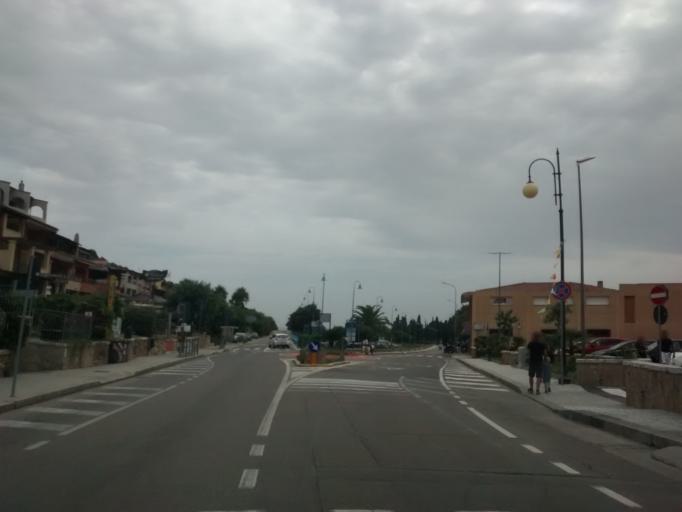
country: IT
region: Sardinia
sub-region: Provincia di Cagliari
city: Villasimius
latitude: 39.1391
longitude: 9.5226
